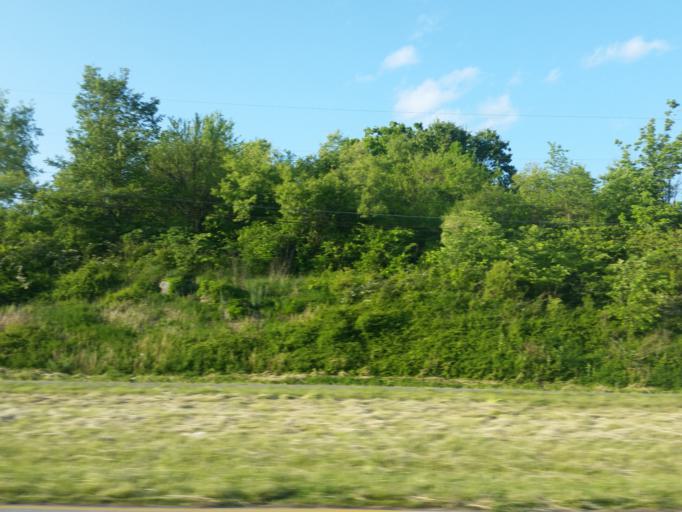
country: US
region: Virginia
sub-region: Washington County
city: Abingdon
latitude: 36.7243
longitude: -82.0196
